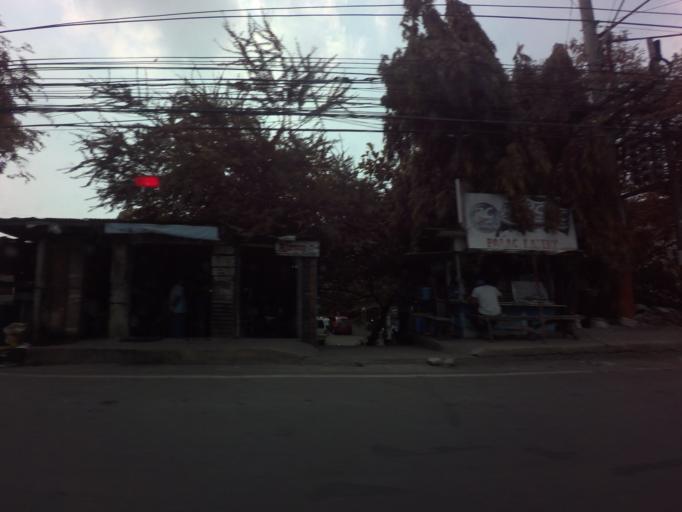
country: PH
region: Calabarzon
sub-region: Province of Rizal
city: Taguig
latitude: 14.4909
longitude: 121.0616
